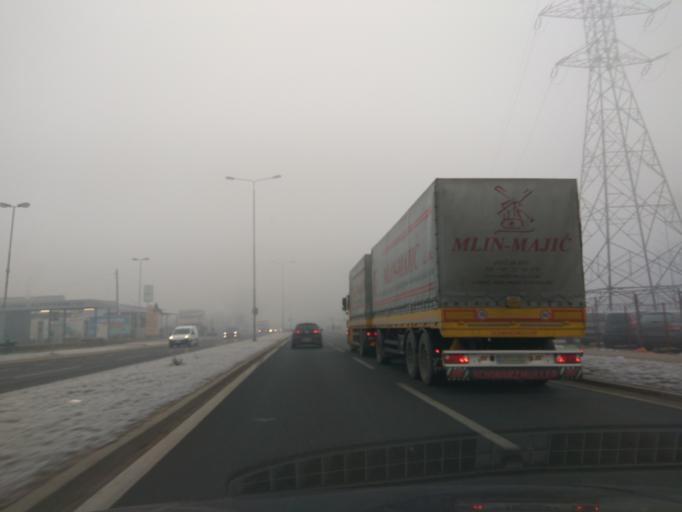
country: BA
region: Federation of Bosnia and Herzegovina
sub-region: Kanton Sarajevo
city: Sarajevo
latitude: 43.8481
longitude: 18.3270
